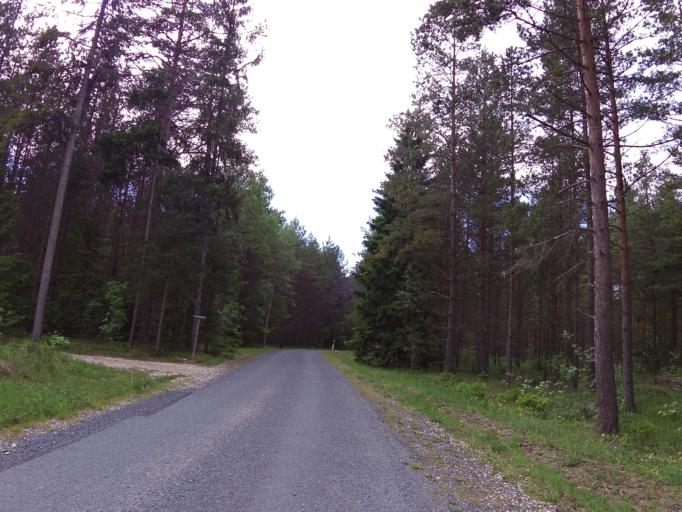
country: EE
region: Harju
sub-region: Paldiski linn
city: Paldiski
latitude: 59.2501
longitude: 23.7671
